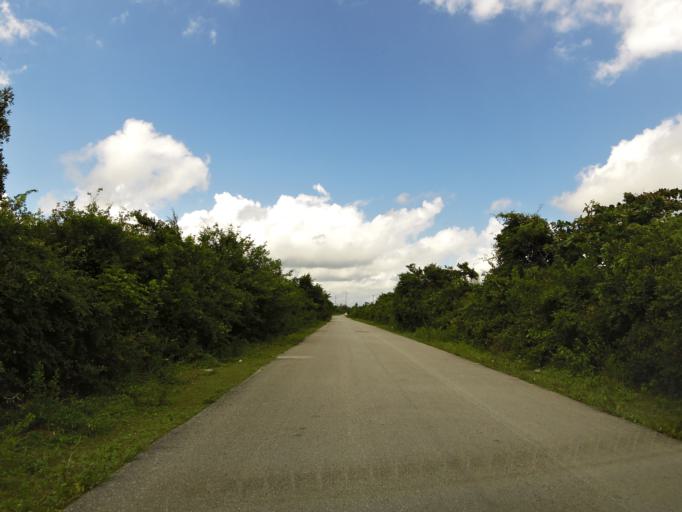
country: TZ
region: Zanzibar Central/South
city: Koani
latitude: -6.1512
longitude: 39.4283
